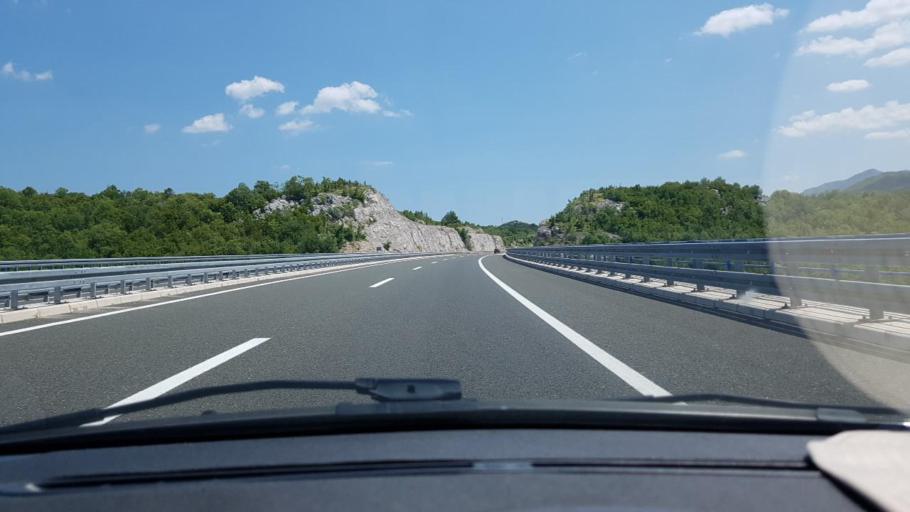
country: HR
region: Splitsko-Dalmatinska
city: Grubine
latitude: 43.3771
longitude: 17.0848
